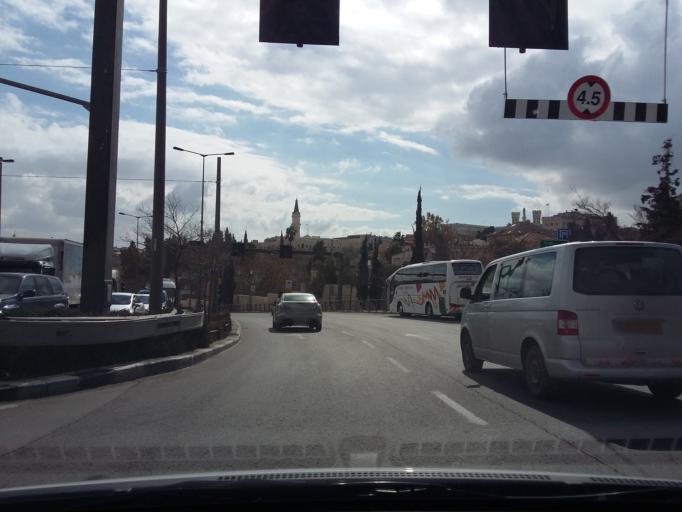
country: PS
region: West Bank
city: East Jerusalem
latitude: 31.7834
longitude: 35.2271
